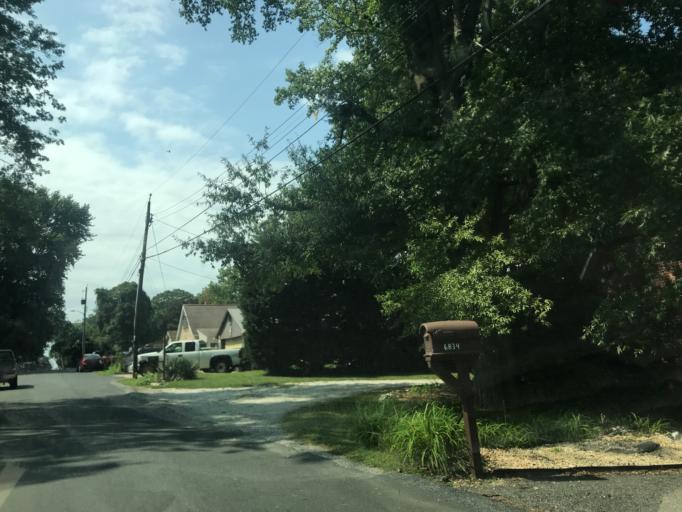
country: US
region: Maryland
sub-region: Baltimore County
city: Bowleys Quarters
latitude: 39.3763
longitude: -76.3634
